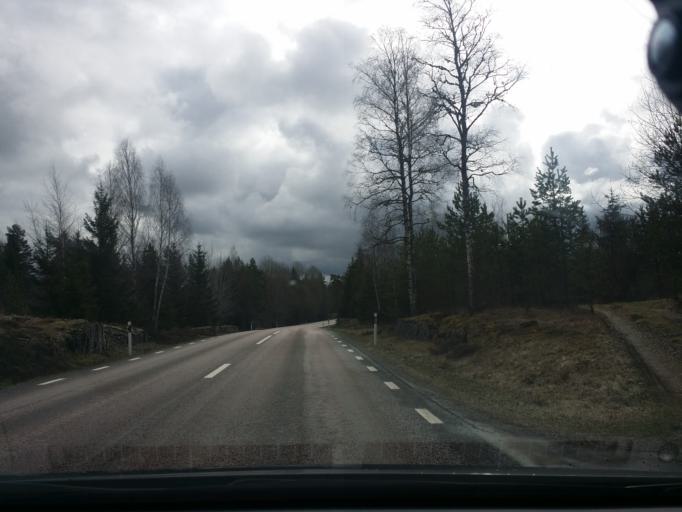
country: SE
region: Uppsala
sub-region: Enkopings Kommun
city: Irsta
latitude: 59.7924
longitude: 16.8266
